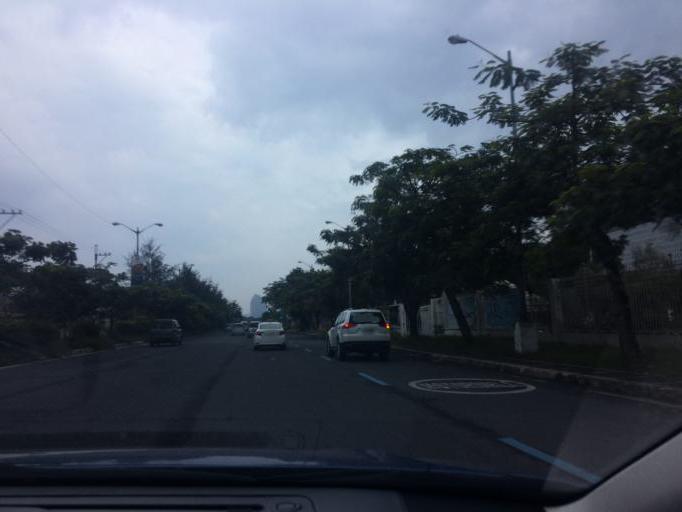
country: PH
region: Metro Manila
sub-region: City of Manila
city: Port Area
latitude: 14.5466
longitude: 120.9872
